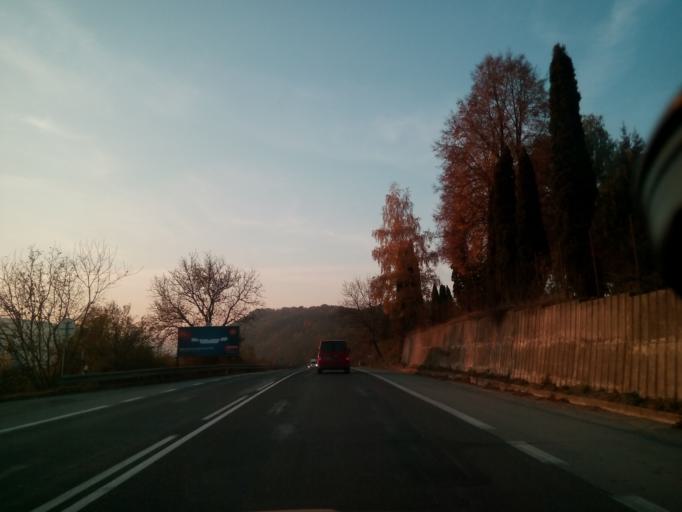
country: SK
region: Presovsky
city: Sabinov
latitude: 49.0066
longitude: 21.0695
